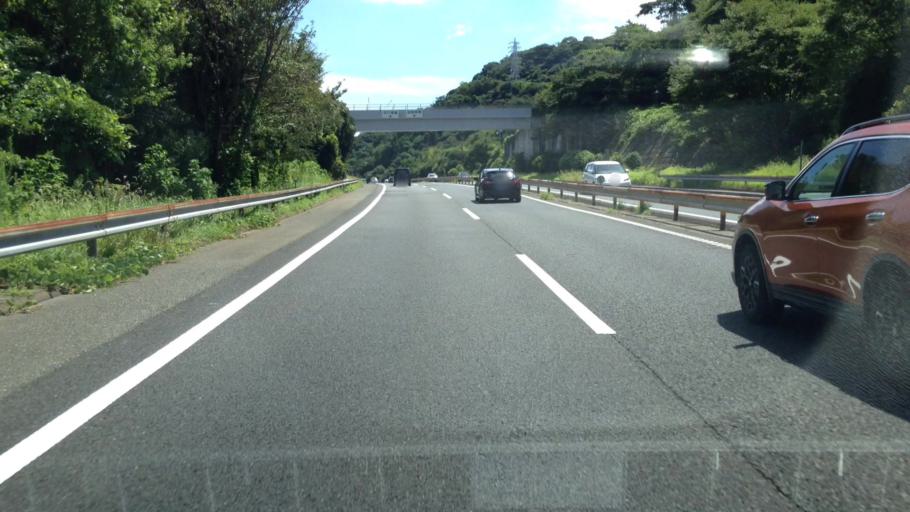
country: JP
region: Kanagawa
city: Yokosuka
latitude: 35.2601
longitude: 139.6337
